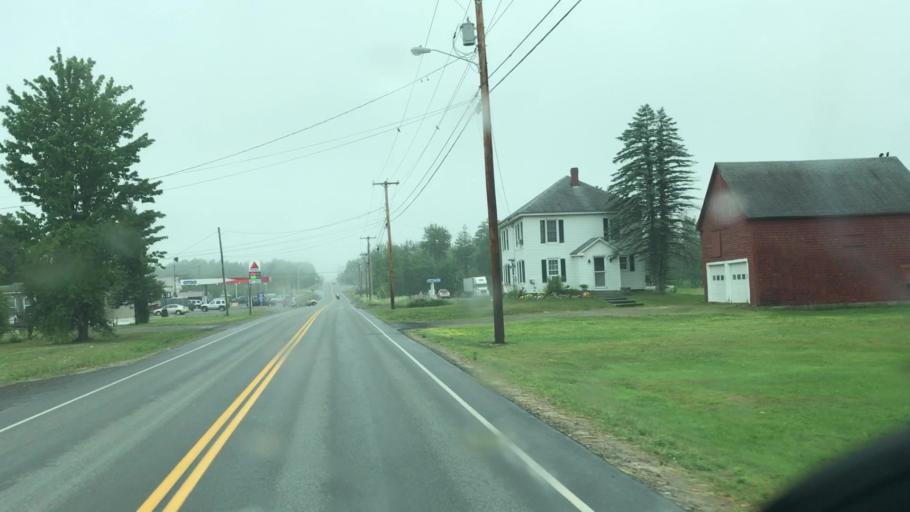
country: US
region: Maine
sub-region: Penobscot County
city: Howland
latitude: 45.2376
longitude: -68.6697
